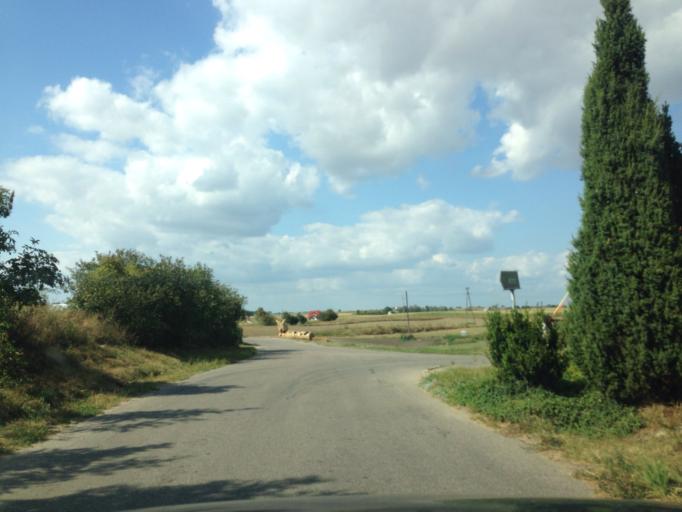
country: PL
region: Kujawsko-Pomorskie
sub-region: Powiat brodnicki
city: Brzozie
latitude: 53.3307
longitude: 19.6617
